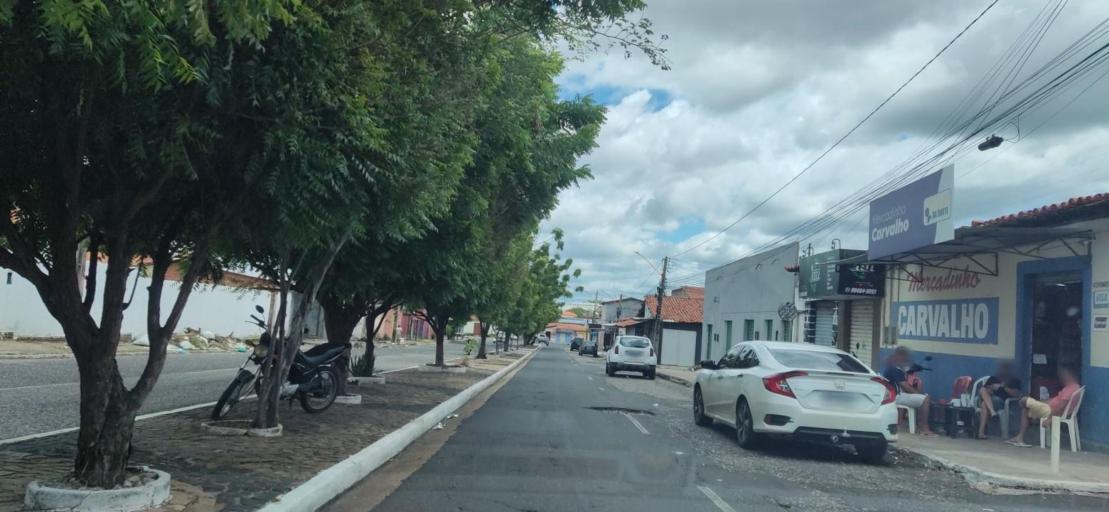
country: BR
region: Piaui
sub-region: Teresina
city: Teresina
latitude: -5.1468
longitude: -42.7800
